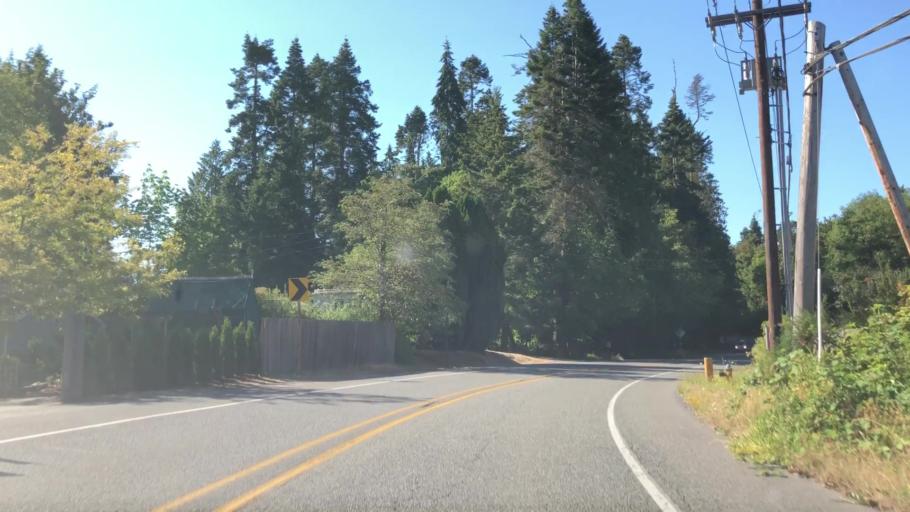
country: US
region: Washington
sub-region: Kitsap County
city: Kingston
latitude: 47.7938
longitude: -122.5059
